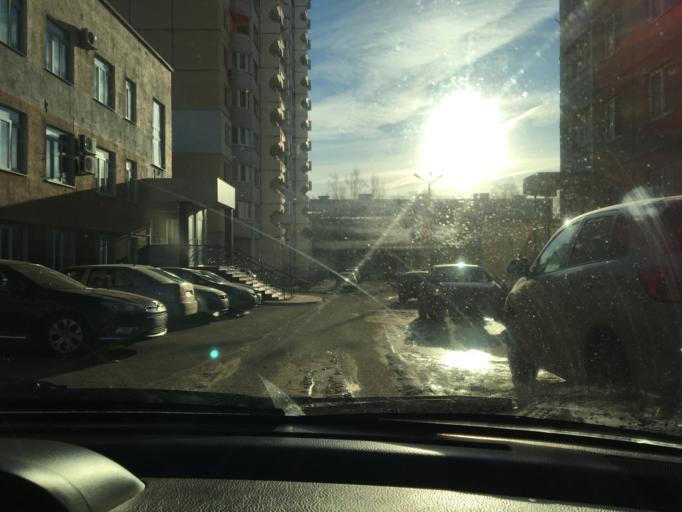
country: RU
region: Tula
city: Tula
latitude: 54.2132
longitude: 37.6038
